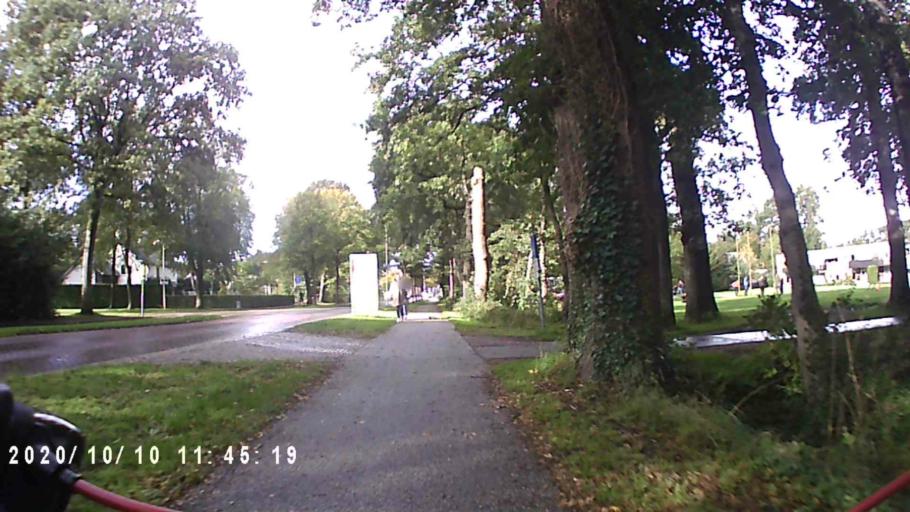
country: NL
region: Friesland
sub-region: Gemeente Smallingerland
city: Boornbergum
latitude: 53.0592
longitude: 6.0839
